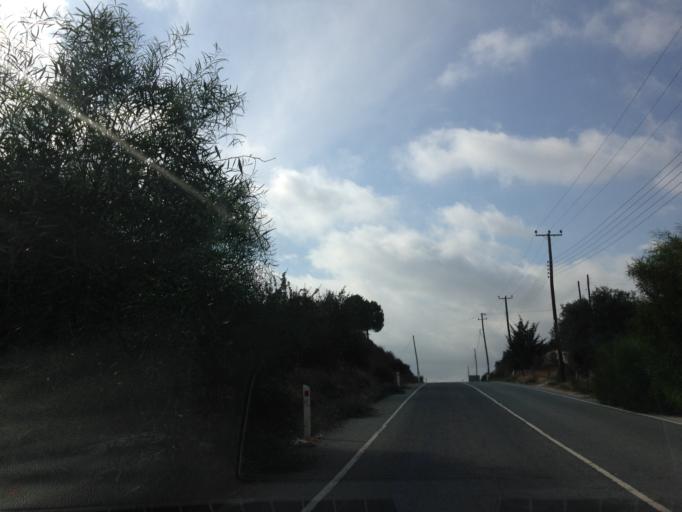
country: CY
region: Limassol
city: Pachna
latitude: 34.7967
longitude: 32.8034
